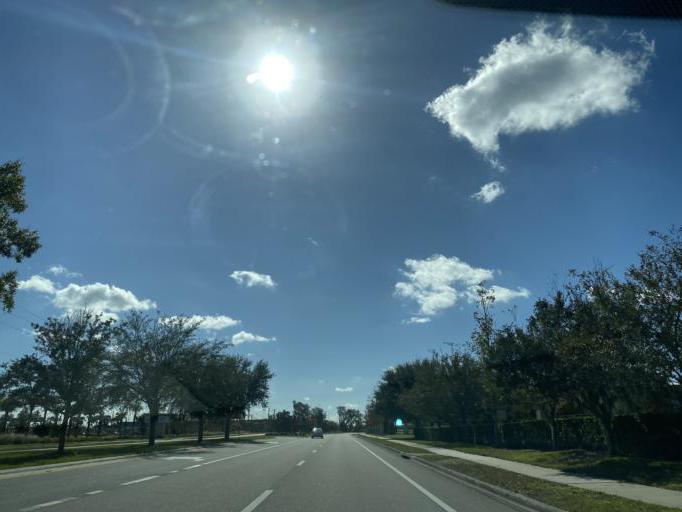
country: US
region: Florida
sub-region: Seminole County
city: Heathrow
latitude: 28.8036
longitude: -81.3481
